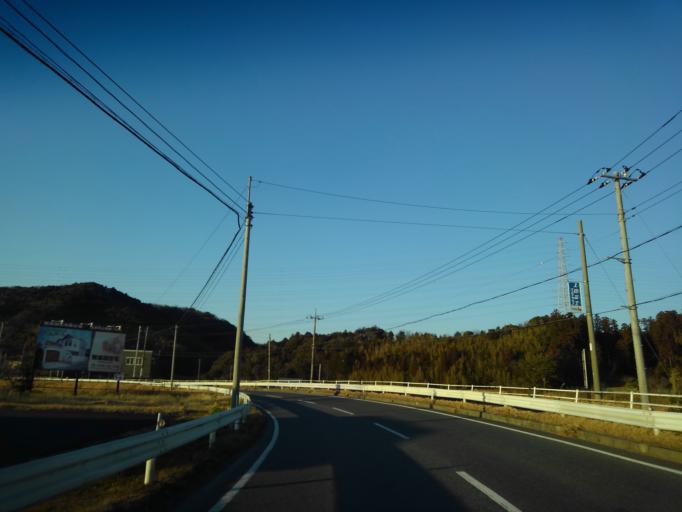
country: JP
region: Chiba
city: Kisarazu
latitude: 35.3039
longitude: 139.9871
